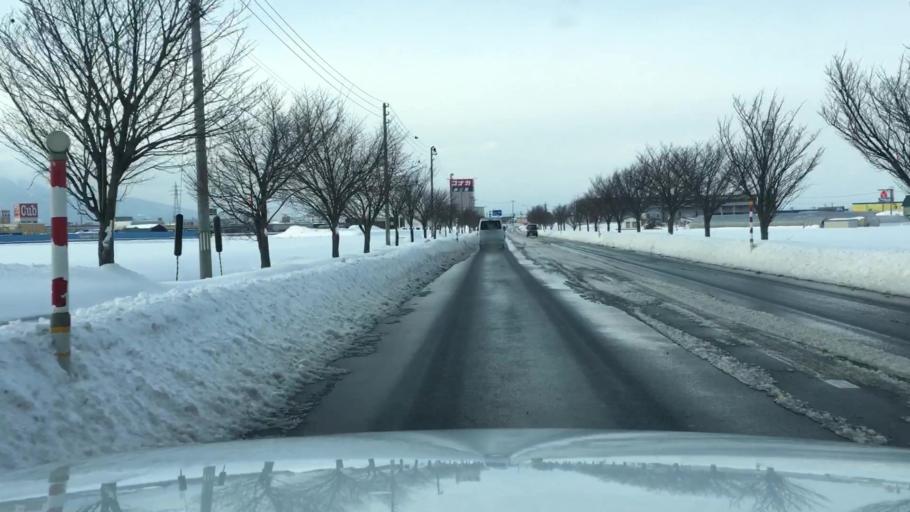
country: JP
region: Aomori
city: Hirosaki
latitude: 40.5959
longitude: 140.5171
